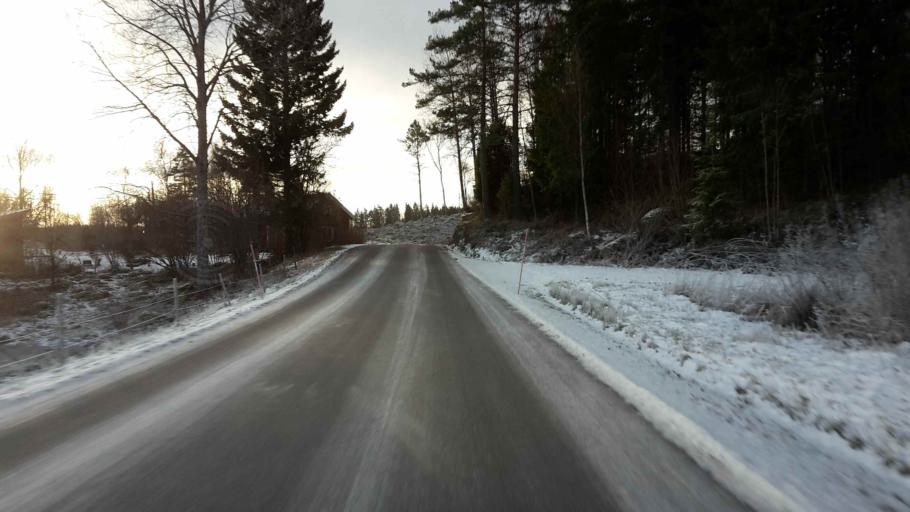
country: SE
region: OEstergoetland
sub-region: Atvidabergs Kommun
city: Atvidaberg
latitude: 58.2573
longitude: 16.1012
